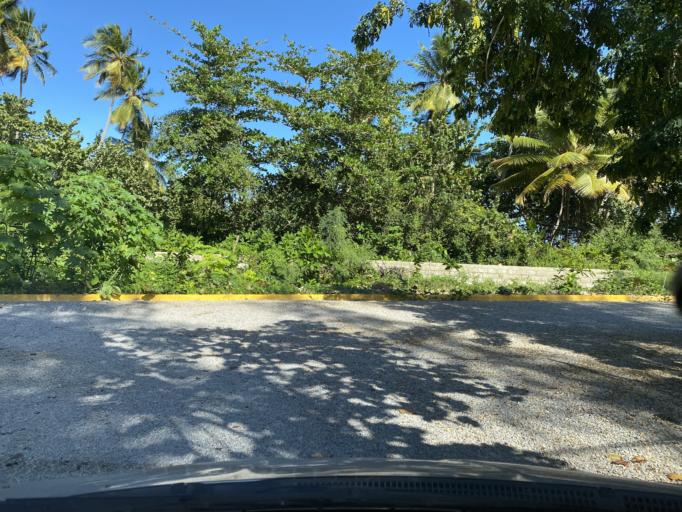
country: DO
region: Samana
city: Las Terrenas
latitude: 19.3248
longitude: -69.5283
